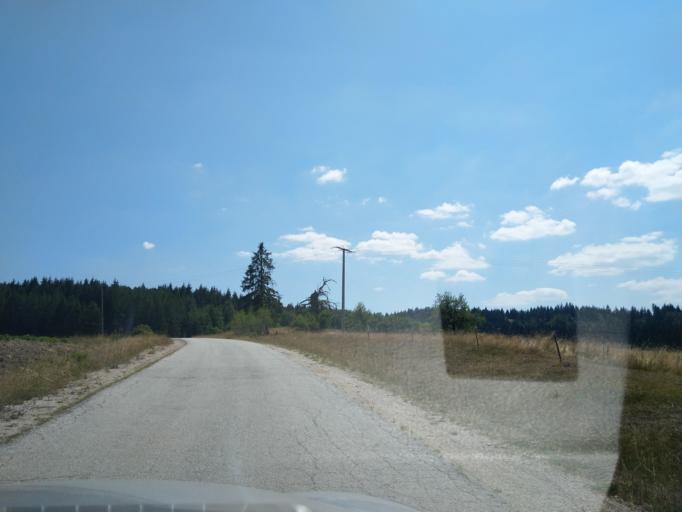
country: RS
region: Central Serbia
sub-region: Zlatiborski Okrug
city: Nova Varos
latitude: 43.4700
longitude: 19.9663
